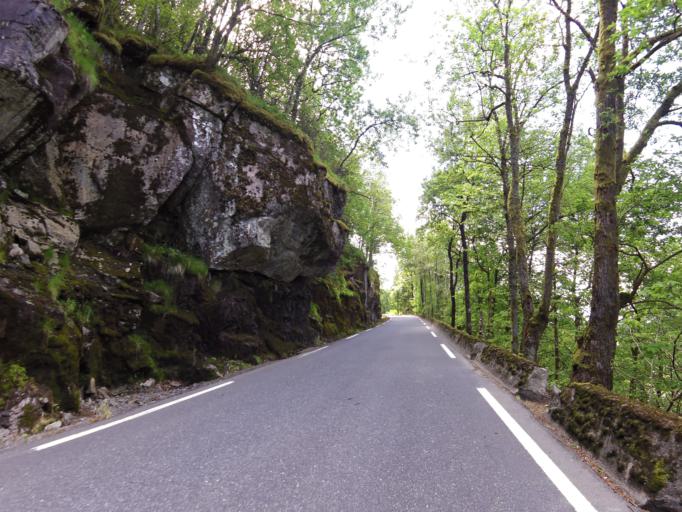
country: NO
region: Vest-Agder
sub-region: Kvinesdal
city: Liknes
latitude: 58.2915
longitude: 6.9406
